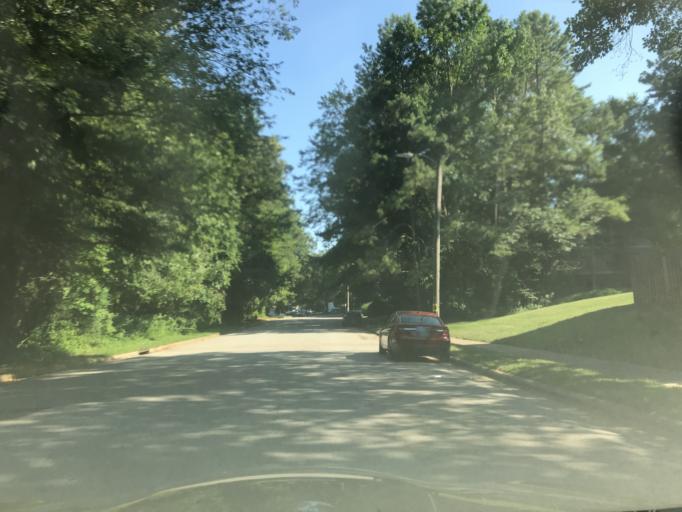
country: US
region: North Carolina
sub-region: Wake County
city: West Raleigh
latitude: 35.8561
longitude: -78.6076
